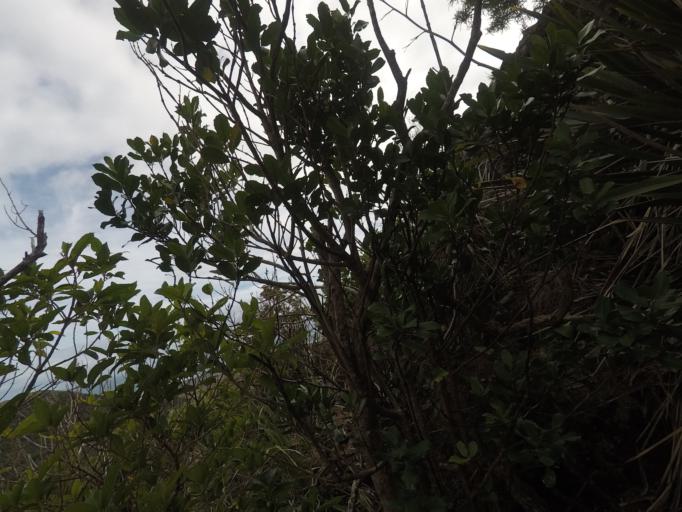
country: NZ
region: Auckland
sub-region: Auckland
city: Titirangi
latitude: -37.0360
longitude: 174.5173
